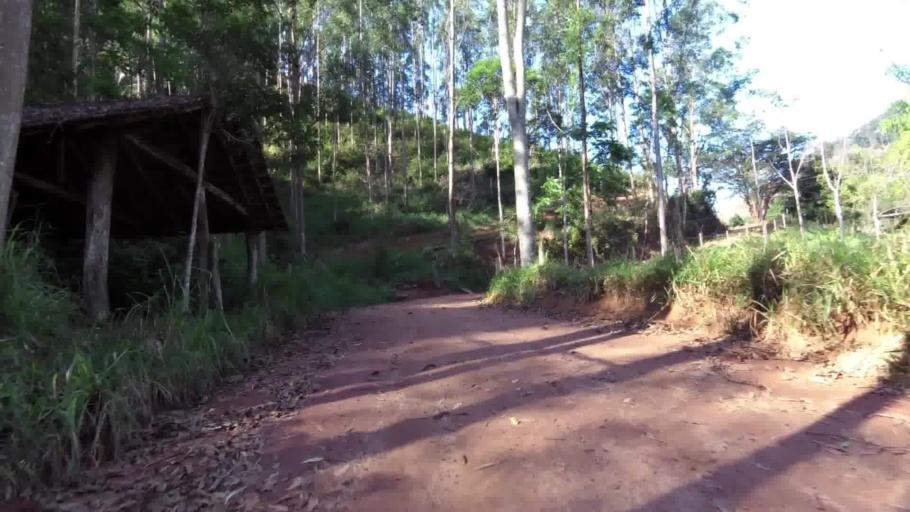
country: BR
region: Espirito Santo
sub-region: Alfredo Chaves
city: Alfredo Chaves
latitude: -20.6070
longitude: -40.7539
